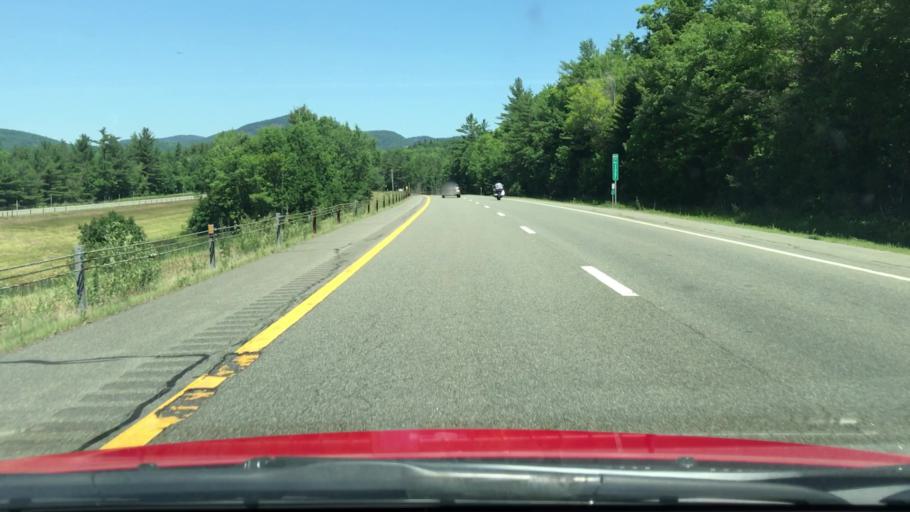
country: US
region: New York
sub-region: Essex County
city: Elizabethtown
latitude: 44.3397
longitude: -73.5327
